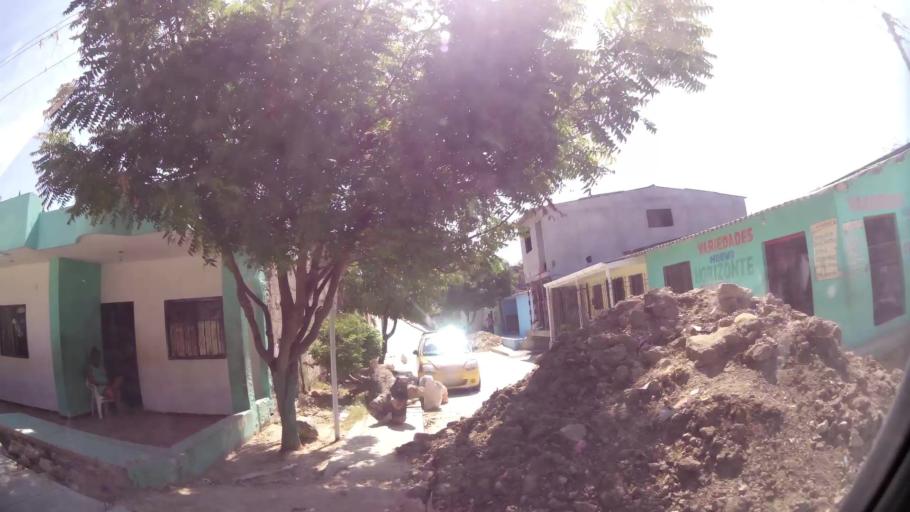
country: CO
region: Atlantico
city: Barranquilla
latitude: 10.9665
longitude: -74.8220
